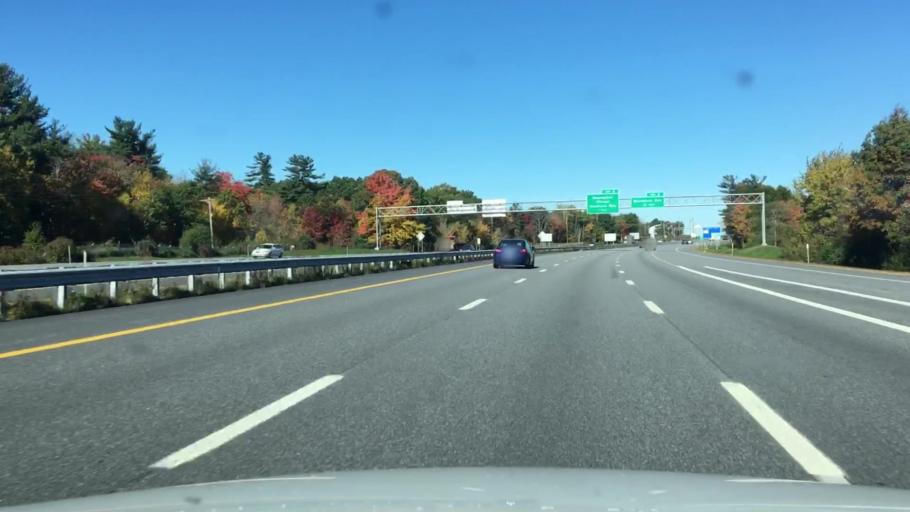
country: US
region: Maine
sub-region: York County
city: South Eliot
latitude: 43.0939
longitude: -70.8062
